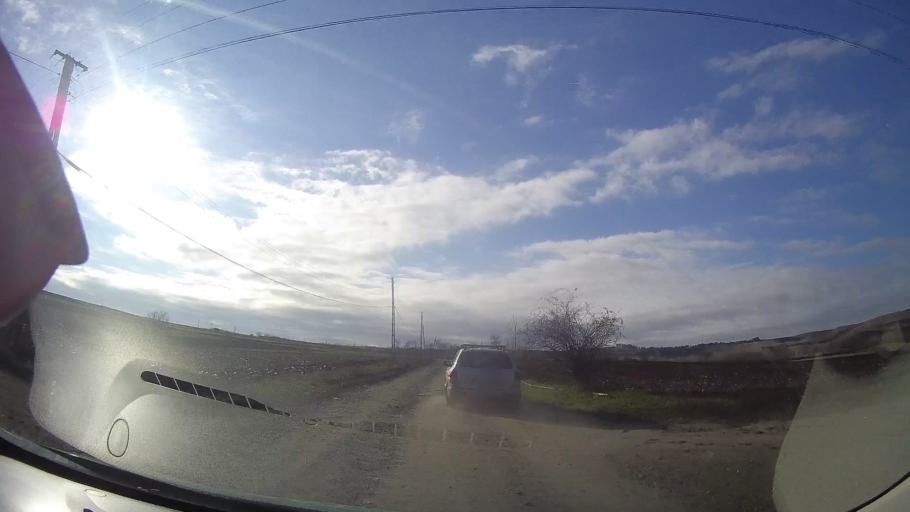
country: RO
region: Mures
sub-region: Comuna Papiu Ilarian
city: Papiu Ilarian
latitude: 46.5708
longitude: 24.2114
